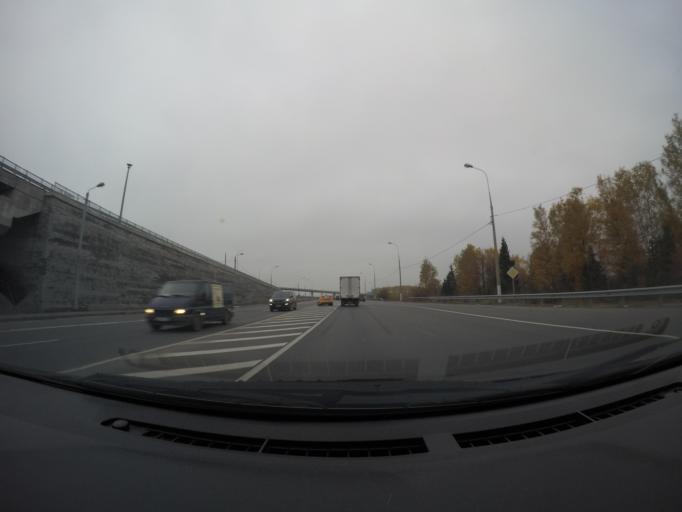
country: RU
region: Moskovskaya
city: Belyye Stolby
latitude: 55.3401
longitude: 37.8180
